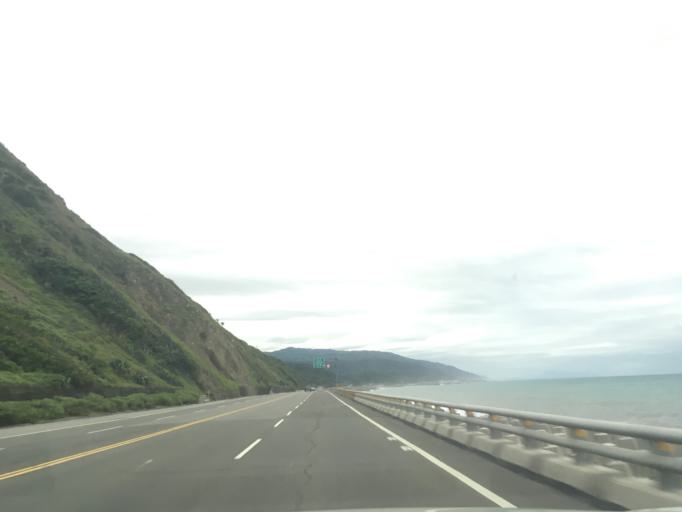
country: TW
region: Taiwan
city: Hengchun
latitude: 22.3134
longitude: 120.8913
